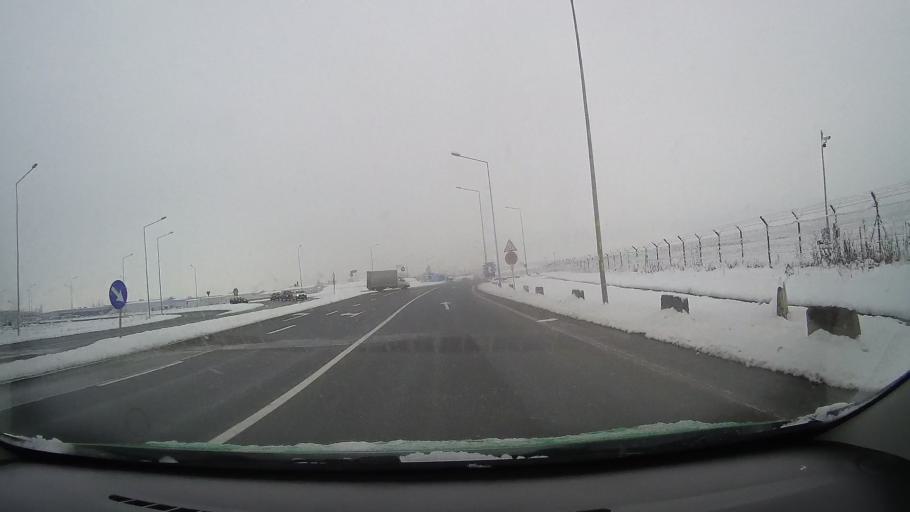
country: RO
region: Sibiu
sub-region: Comuna Cristian
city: Cristian
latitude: 45.7884
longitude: 24.0766
